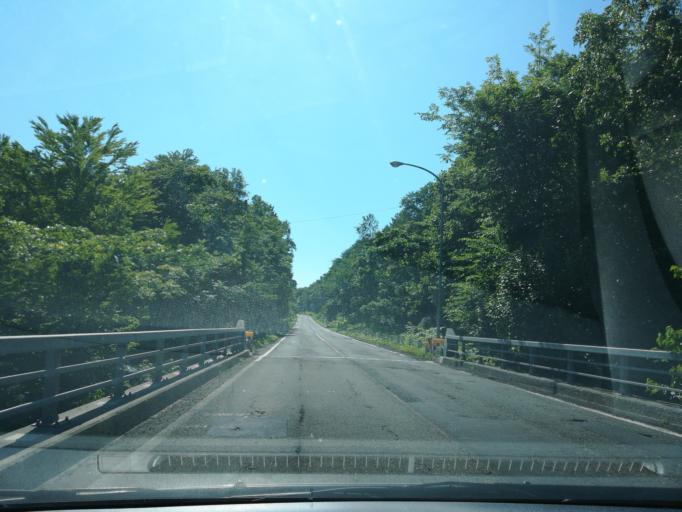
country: JP
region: Hokkaido
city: Chitose
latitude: 42.9100
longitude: 141.9423
